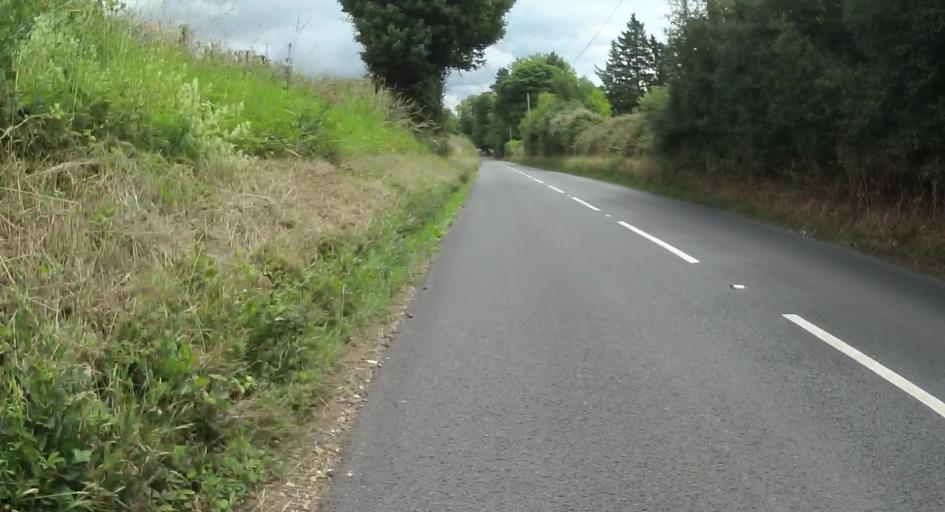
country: GB
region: England
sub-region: Surrey
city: Farnham
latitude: 51.2155
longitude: -0.8369
